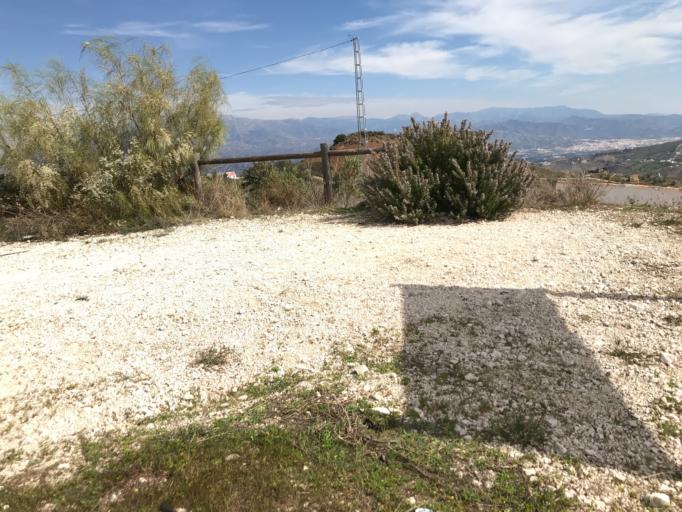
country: ES
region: Andalusia
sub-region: Provincia de Malaga
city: Almachar
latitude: 36.7816
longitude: -4.2236
